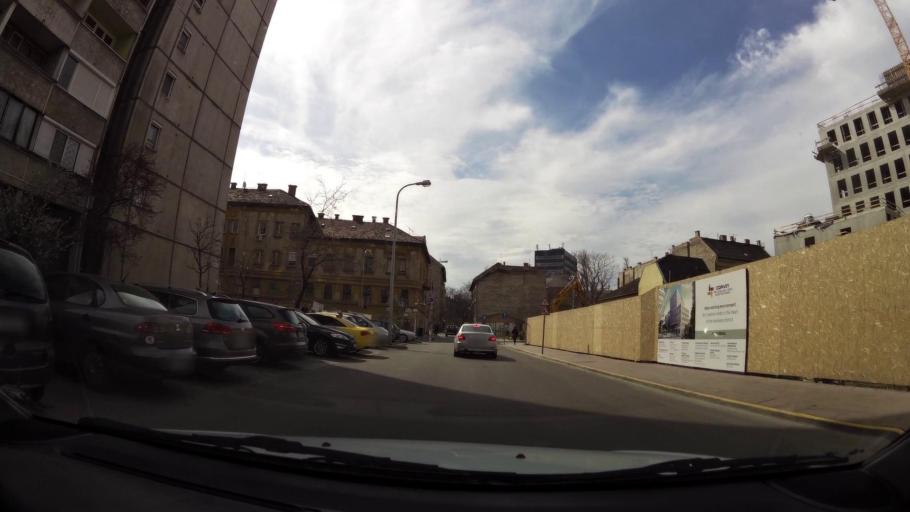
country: HU
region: Budapest
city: Budapest VIII. keruelet
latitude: 47.4855
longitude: 19.0801
